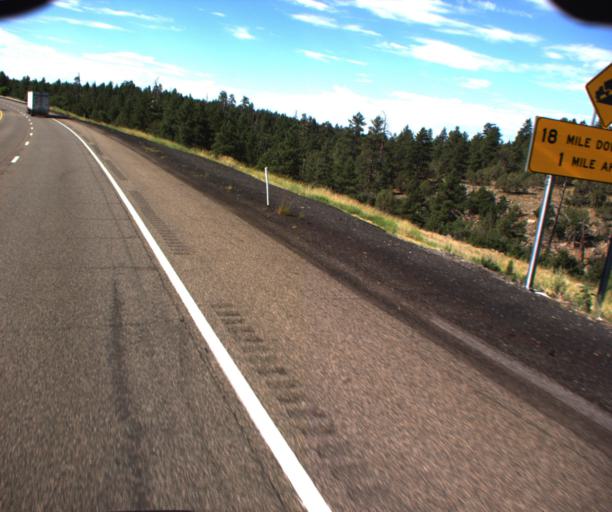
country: US
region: Arizona
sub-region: Yavapai County
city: Village of Oak Creek (Big Park)
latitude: 34.8200
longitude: -111.6137
